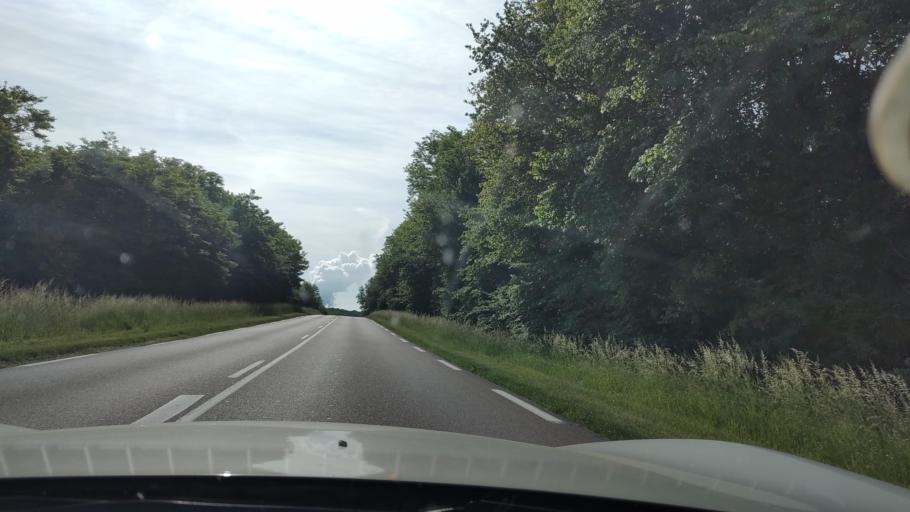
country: FR
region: Ile-de-France
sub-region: Departement de Seine-et-Marne
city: Sourdun
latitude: 48.5327
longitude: 3.3778
